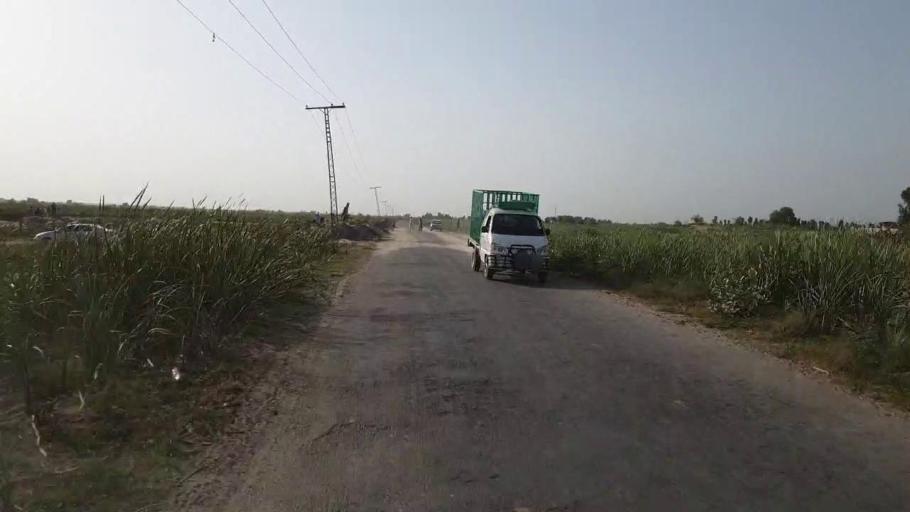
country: PK
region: Sindh
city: Jam Sahib
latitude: 26.4124
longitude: 68.8741
